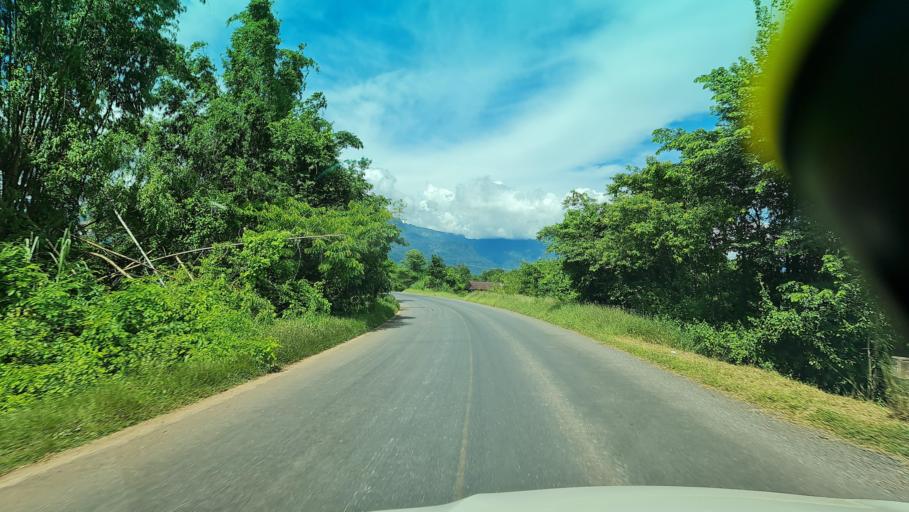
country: LA
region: Bolikhamxai
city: Pakkading
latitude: 18.2990
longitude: 104.1067
